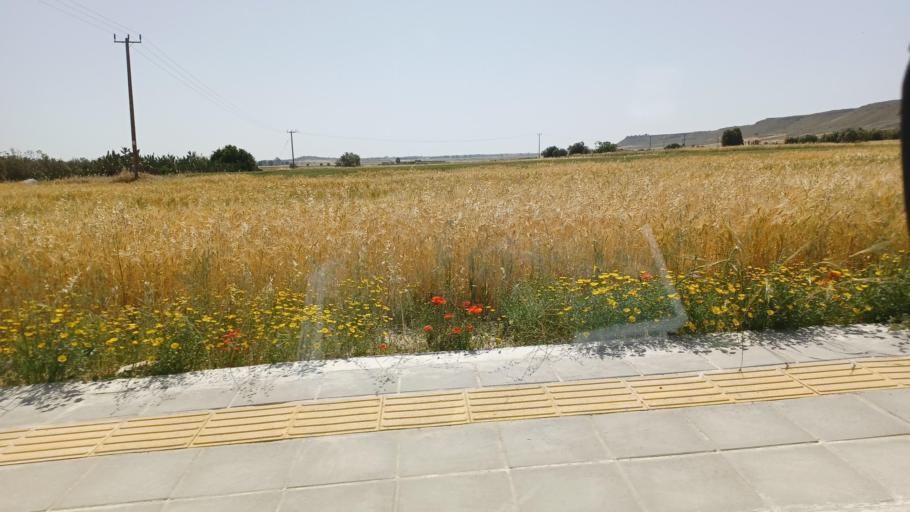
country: CY
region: Lefkosia
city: Mammari
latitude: 35.1822
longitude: 33.2094
